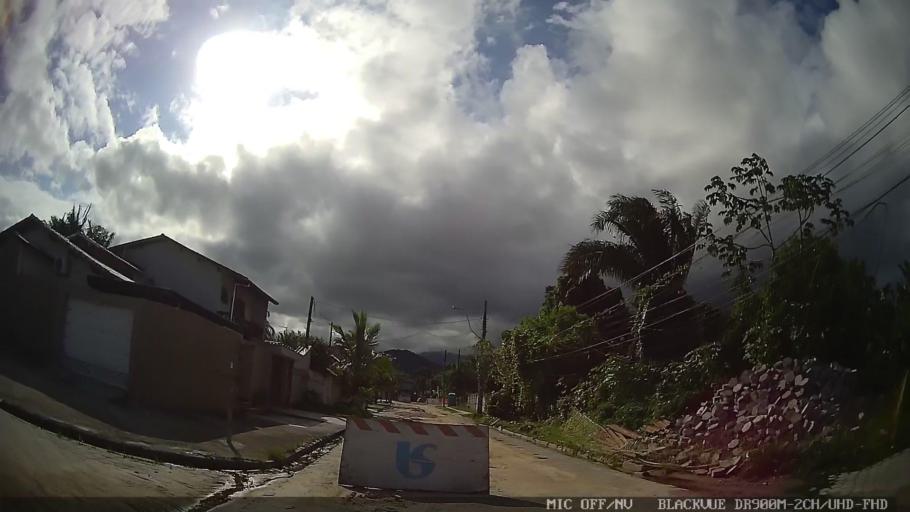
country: BR
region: Sao Paulo
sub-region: Caraguatatuba
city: Caraguatatuba
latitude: -23.6405
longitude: -45.4424
